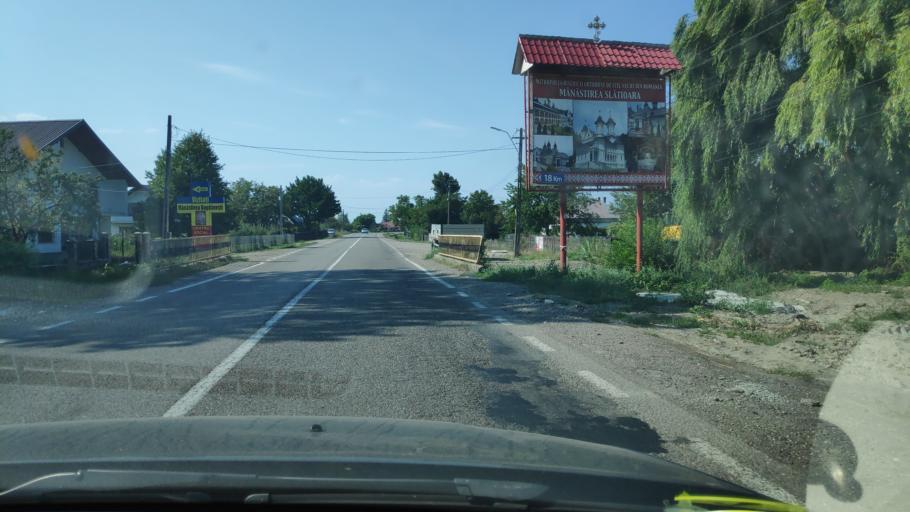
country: RO
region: Suceava
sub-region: Comuna Vadu Moldovei
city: Dumbravita
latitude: 47.3807
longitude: 26.3170
